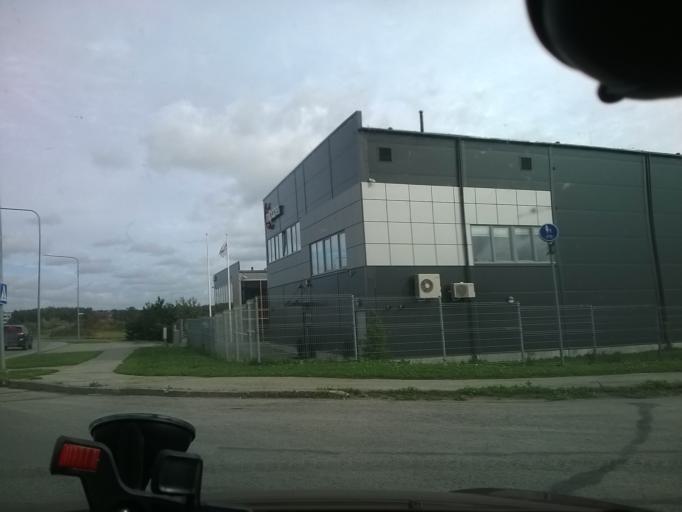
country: EE
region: Harju
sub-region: Tallinna linn
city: Tallinn
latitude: 59.3927
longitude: 24.8170
